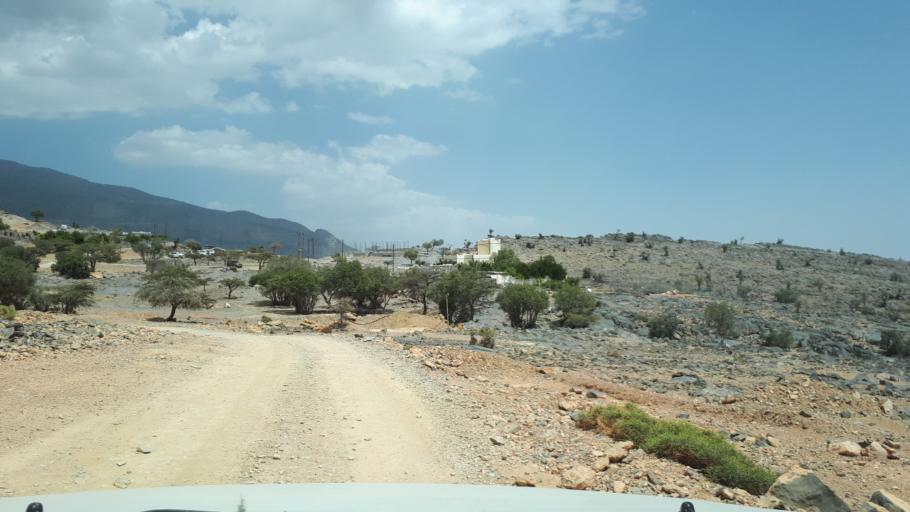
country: OM
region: Muhafazat ad Dakhiliyah
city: Bahla'
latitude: 23.1937
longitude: 57.1988
